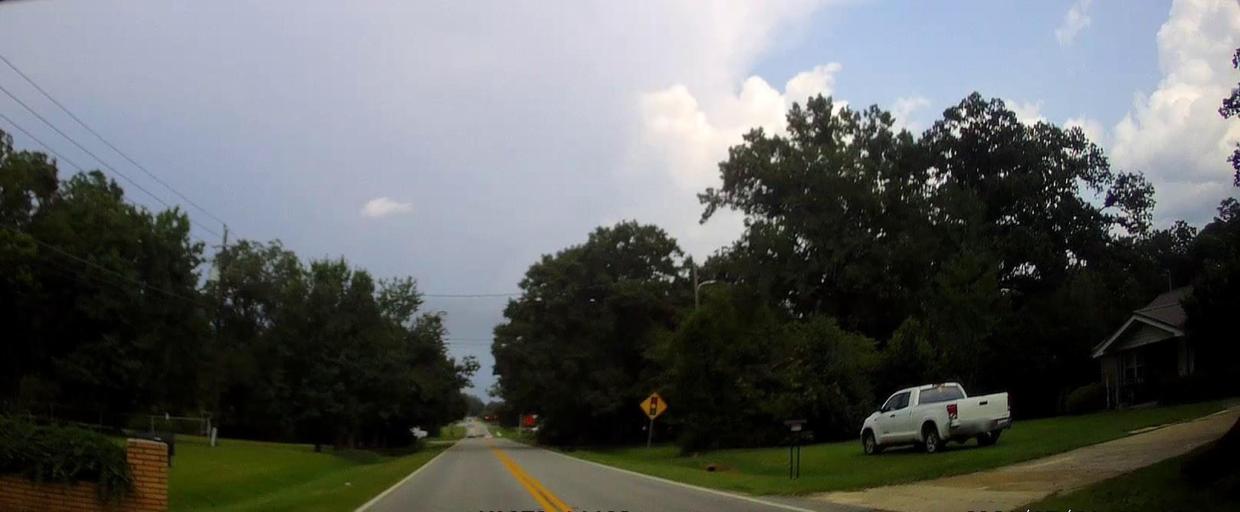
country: US
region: Georgia
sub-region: Houston County
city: Robins Air Force Base
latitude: 32.5683
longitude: -83.5969
